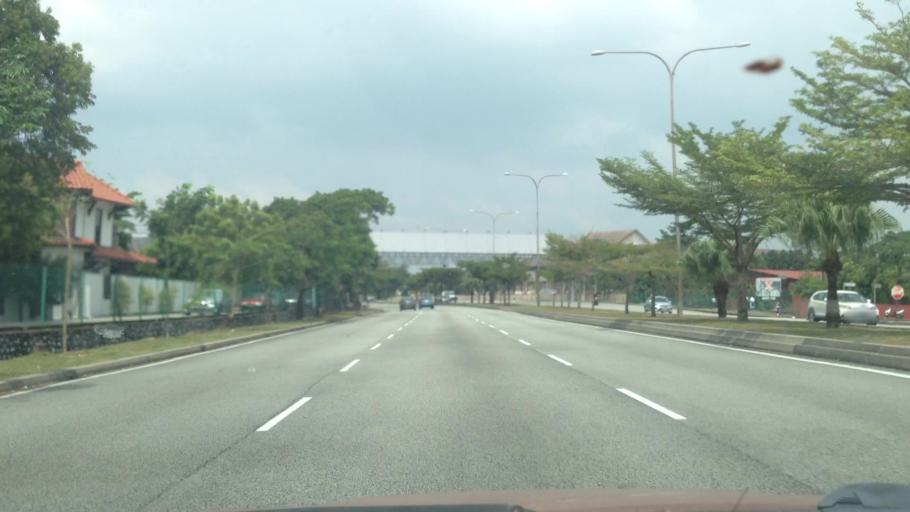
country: MY
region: Selangor
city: Subang Jaya
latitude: 3.0565
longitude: 101.5776
